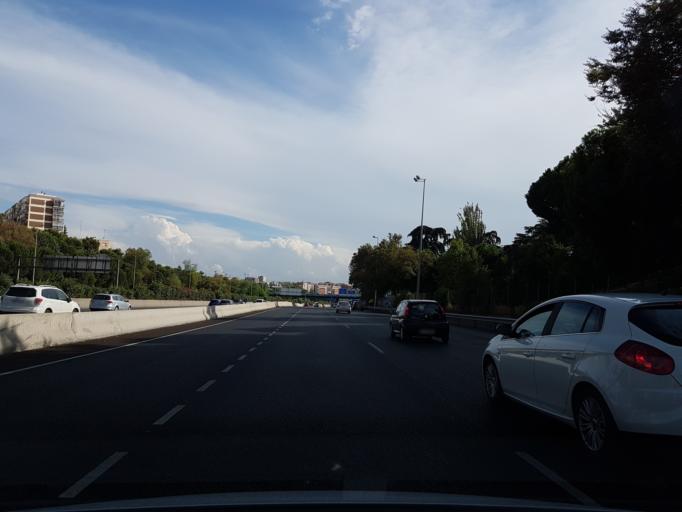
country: ES
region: Madrid
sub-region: Provincia de Madrid
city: Moratalaz
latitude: 40.4252
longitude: -3.6600
